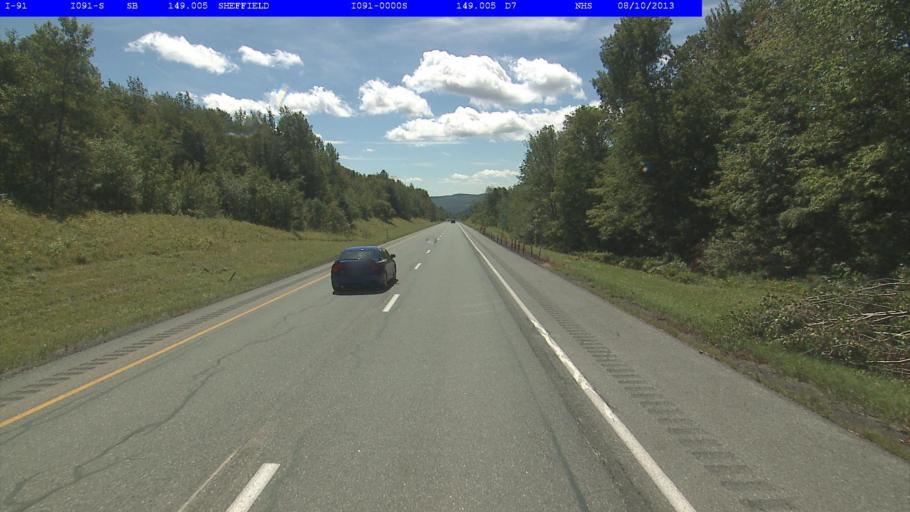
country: US
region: Vermont
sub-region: Caledonia County
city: Lyndonville
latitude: 44.6502
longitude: -72.1343
